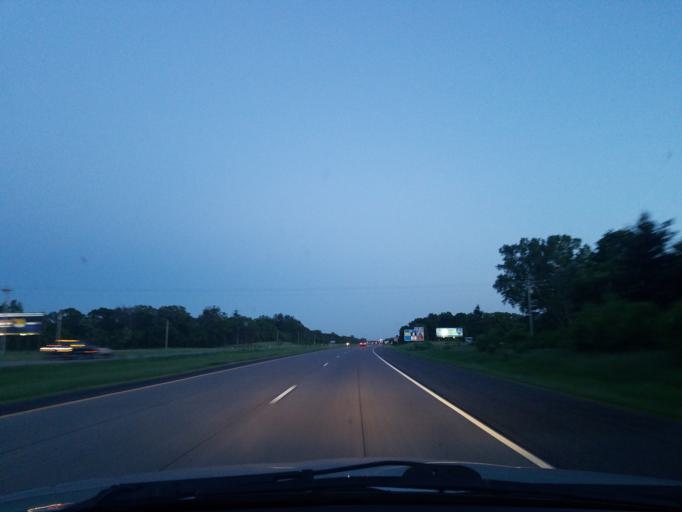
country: US
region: Minnesota
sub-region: Chisago County
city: North Branch
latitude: 45.5291
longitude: -92.9911
